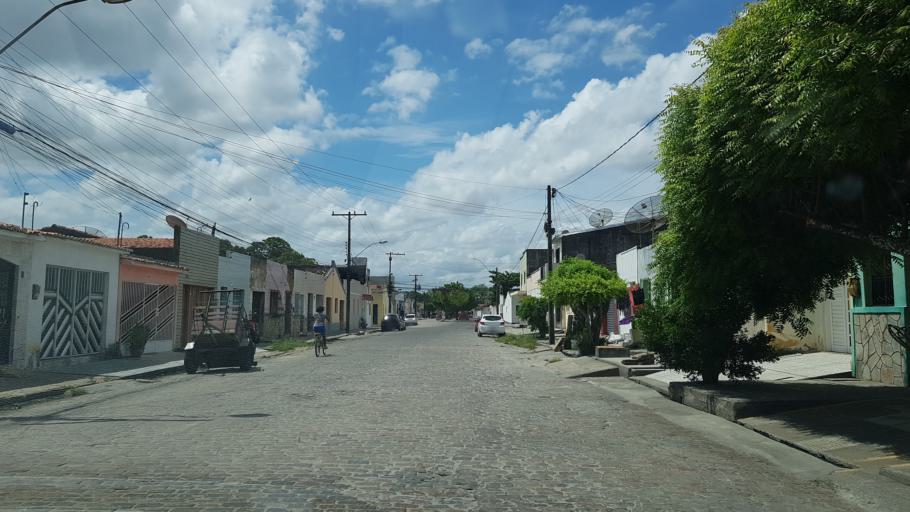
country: BR
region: Alagoas
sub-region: Penedo
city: Penedo
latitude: -10.2793
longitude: -36.5644
